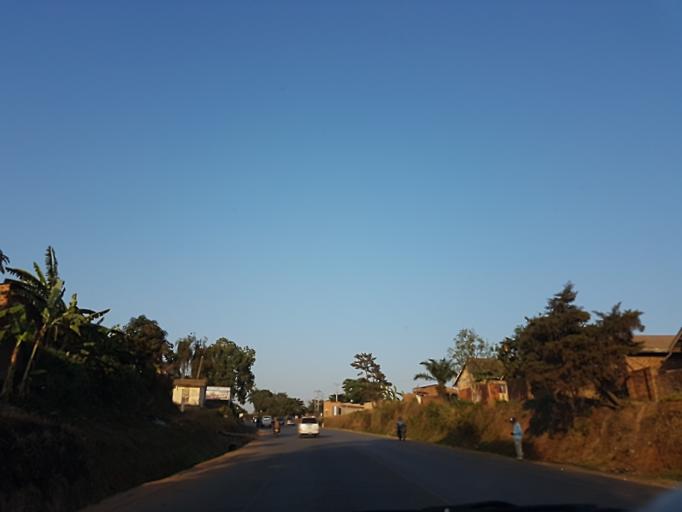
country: UG
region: Central Region
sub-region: Wakiso District
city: Kireka
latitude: 0.4082
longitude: 32.5932
